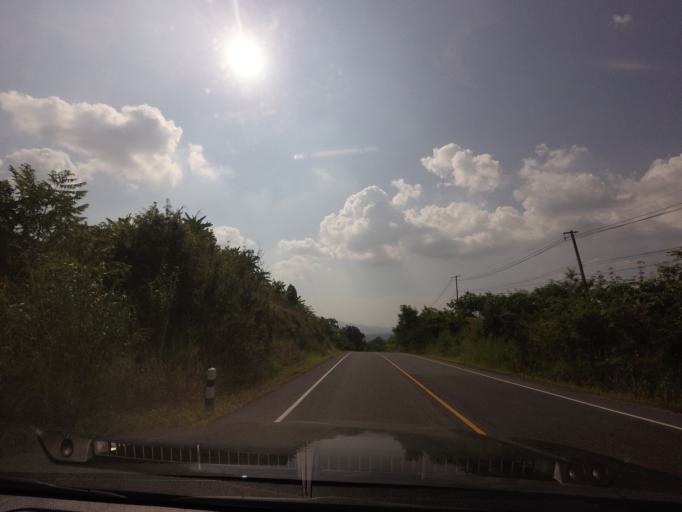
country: TH
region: Nan
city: Santi Suk
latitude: 18.9801
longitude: 100.9577
